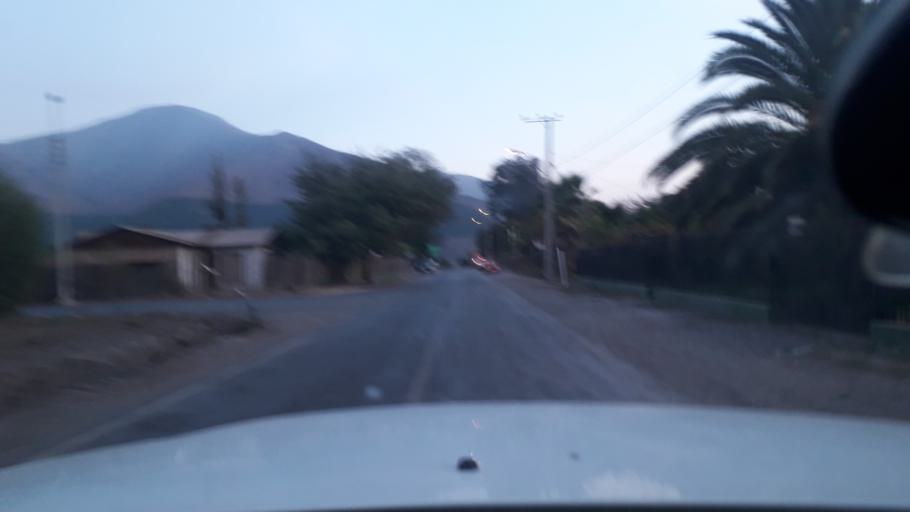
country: CL
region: Valparaiso
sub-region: Provincia de San Felipe
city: Llaillay
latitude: -32.8254
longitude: -71.0301
